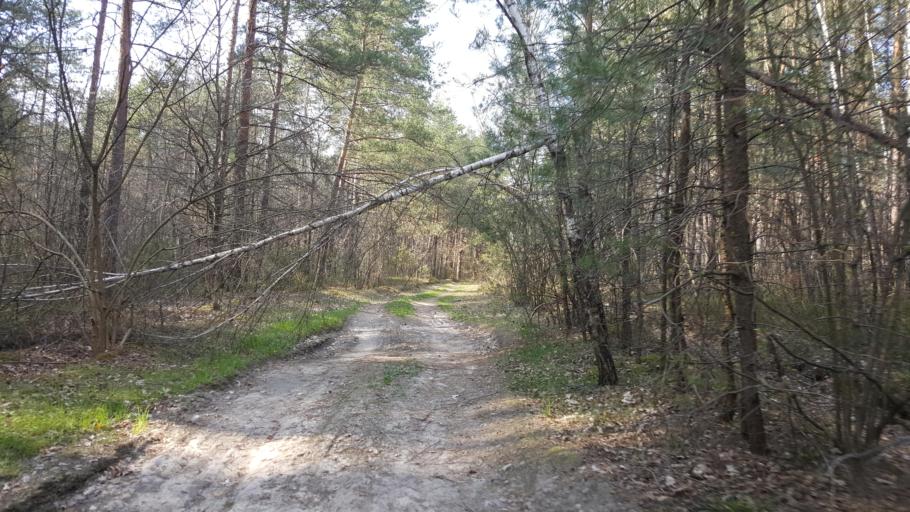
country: BY
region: Brest
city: Kamyanyets
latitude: 52.3367
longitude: 23.8506
